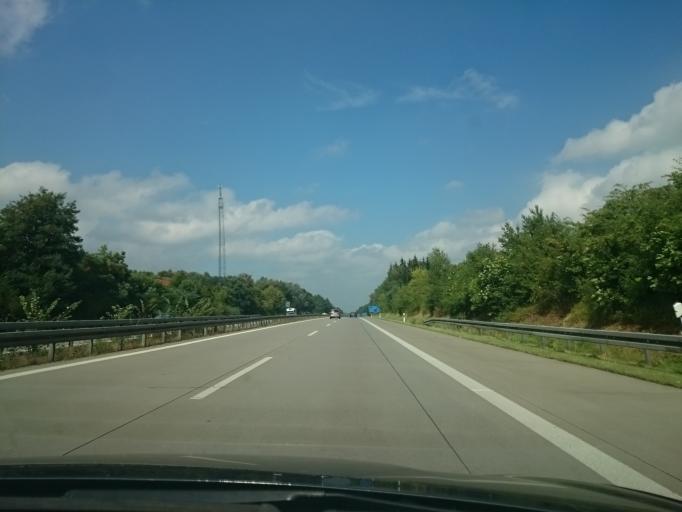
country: DE
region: Brandenburg
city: Bernau bei Berlin
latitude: 52.6947
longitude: 13.5563
